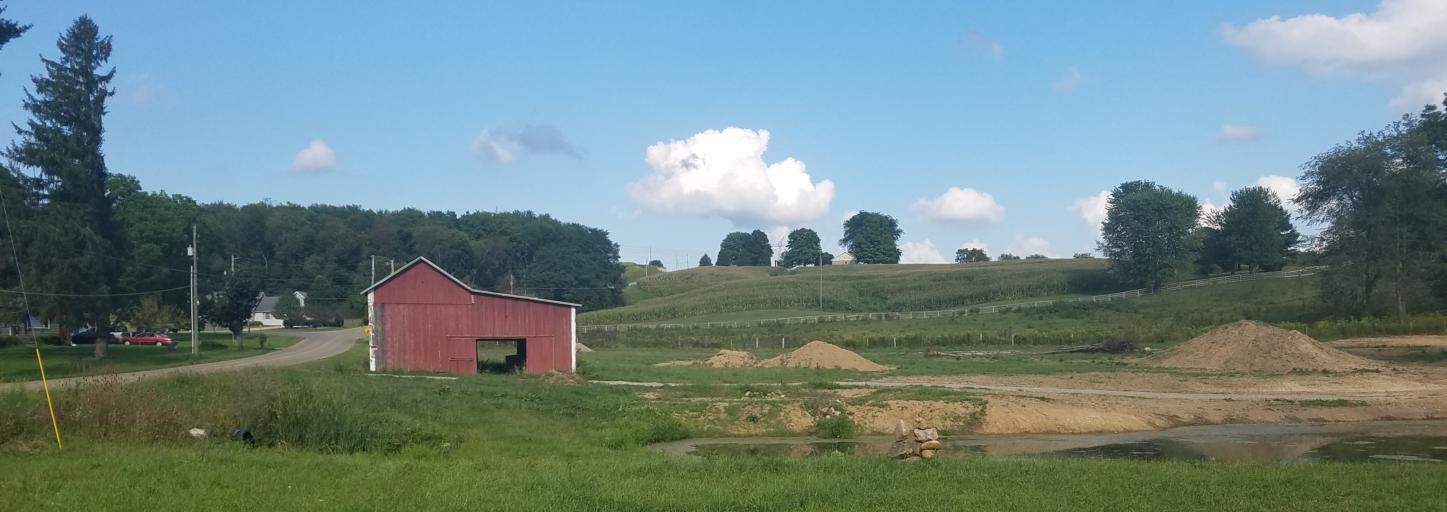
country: US
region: Ohio
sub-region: Knox County
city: Fredericktown
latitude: 40.4852
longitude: -82.5363
